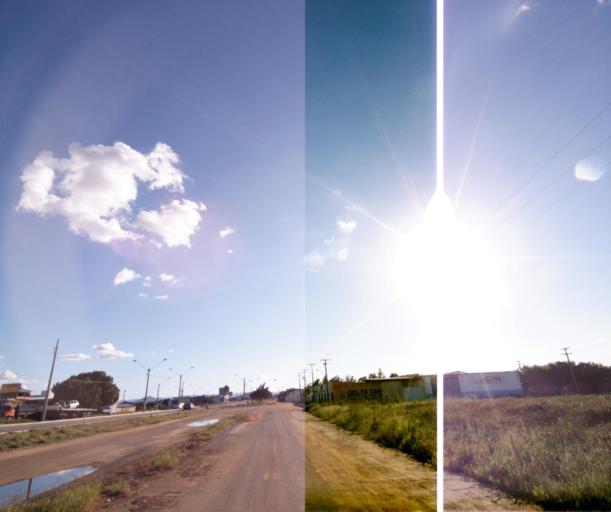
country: BR
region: Bahia
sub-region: Guanambi
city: Guanambi
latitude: -14.2056
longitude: -42.7611
